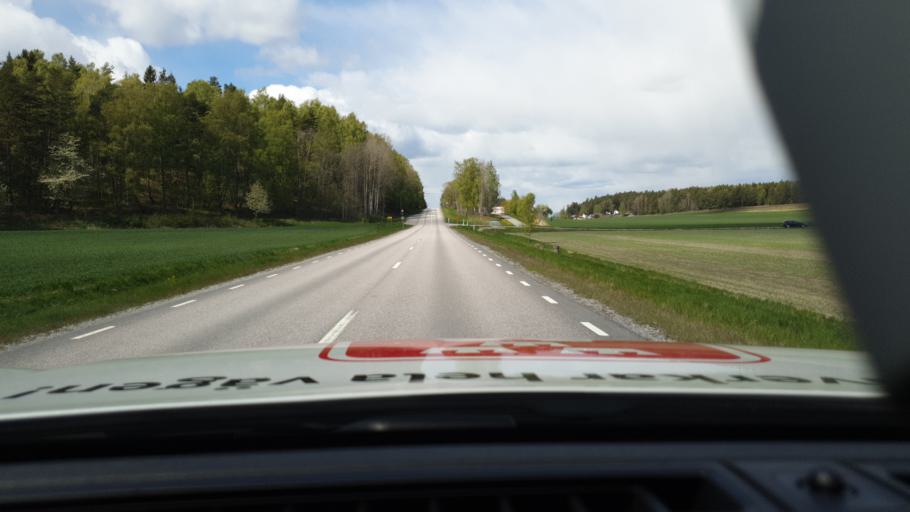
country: SE
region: Stockholm
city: Stenhamra
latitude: 59.3632
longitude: 17.6162
